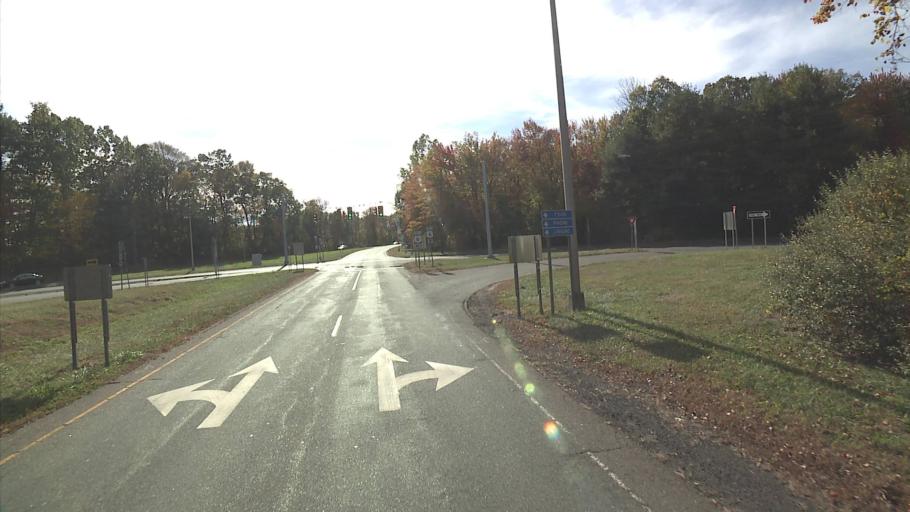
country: US
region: Connecticut
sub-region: Hartford County
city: Farmington
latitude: 41.7183
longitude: -72.7974
